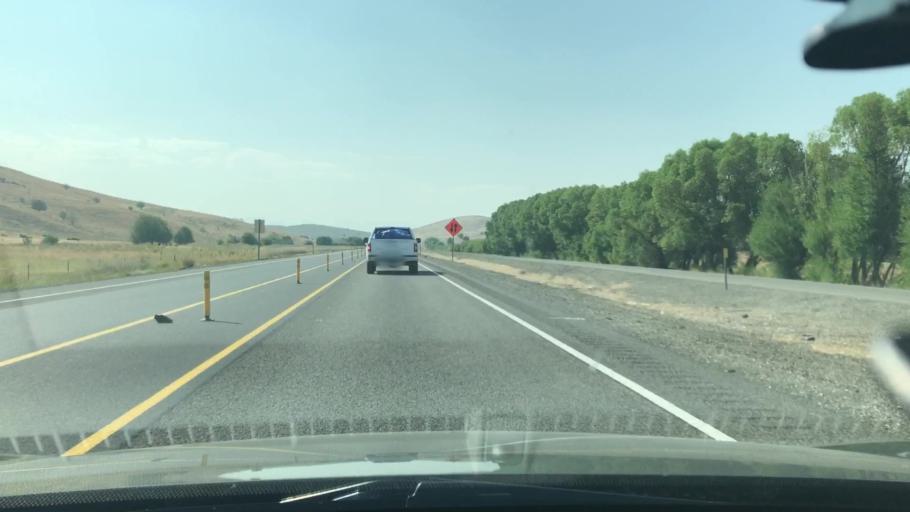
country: US
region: Oregon
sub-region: Baker County
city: Baker City
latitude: 44.6764
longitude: -117.6413
